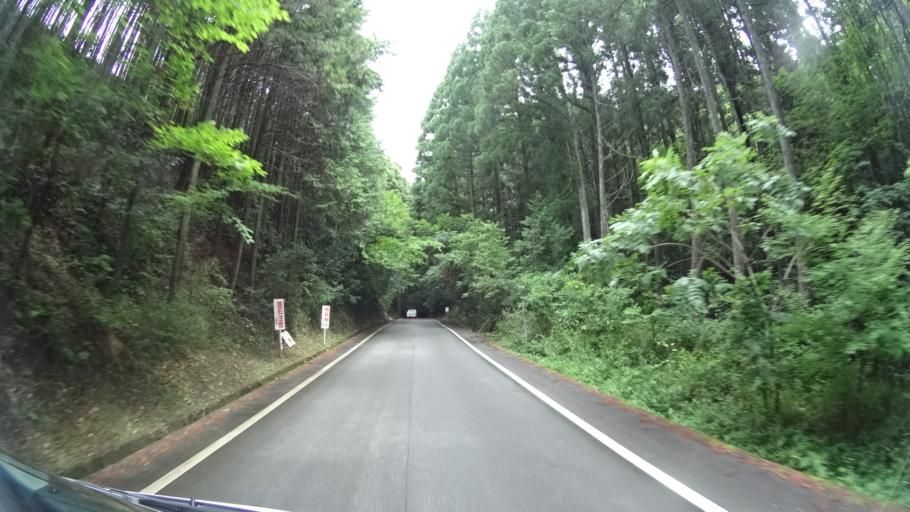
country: JP
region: Kyoto
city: Kameoka
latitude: 35.0839
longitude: 135.4873
